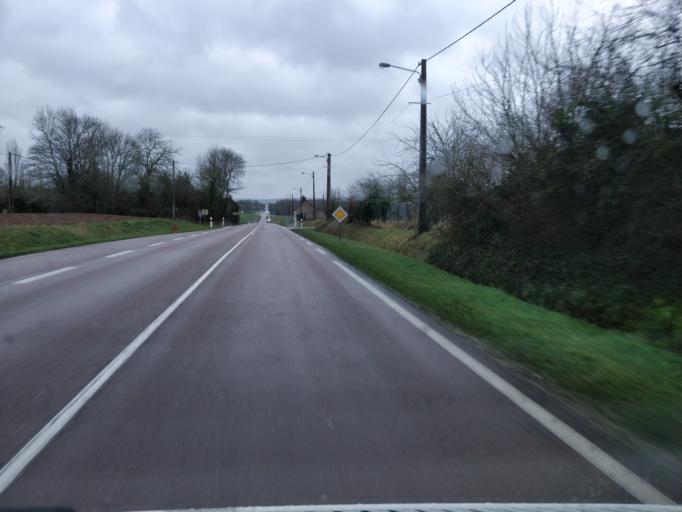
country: FR
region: Champagne-Ardenne
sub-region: Departement de l'Aube
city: Aix-en-Othe
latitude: 48.2352
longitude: 3.5923
